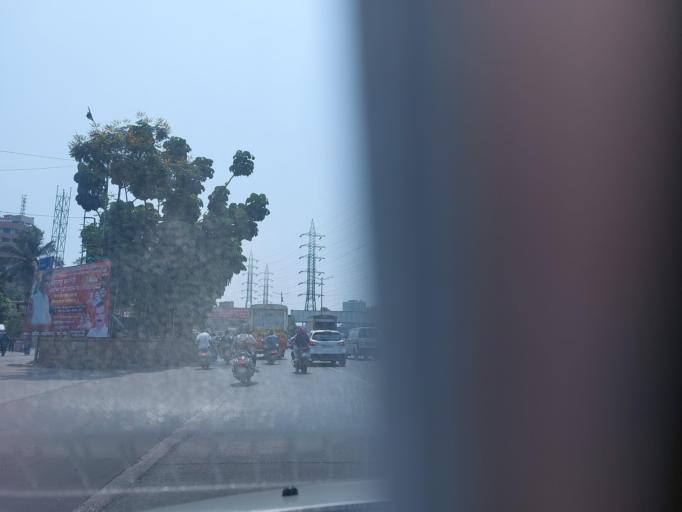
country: IN
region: Maharashtra
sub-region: Mumbai Suburban
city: Mumbai
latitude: 19.0538
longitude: 72.8834
